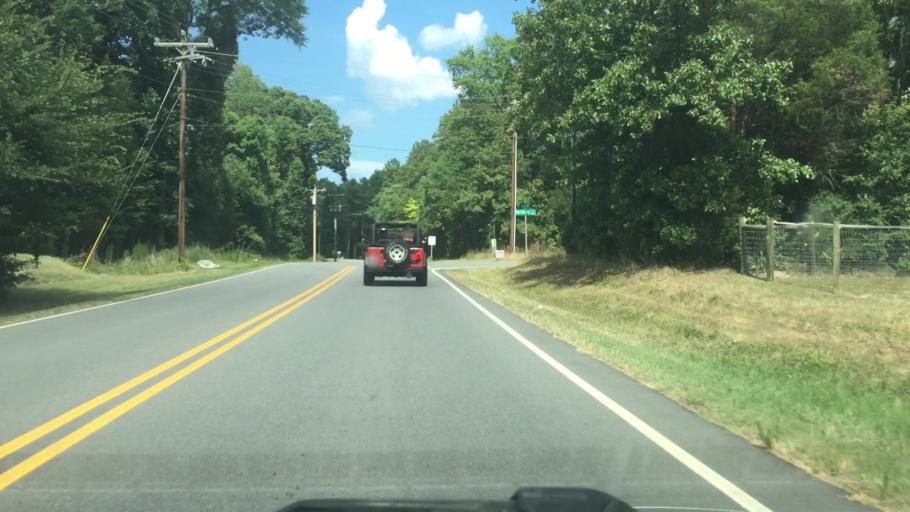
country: US
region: North Carolina
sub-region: Mecklenburg County
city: Huntersville
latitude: 35.4309
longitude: -80.7328
